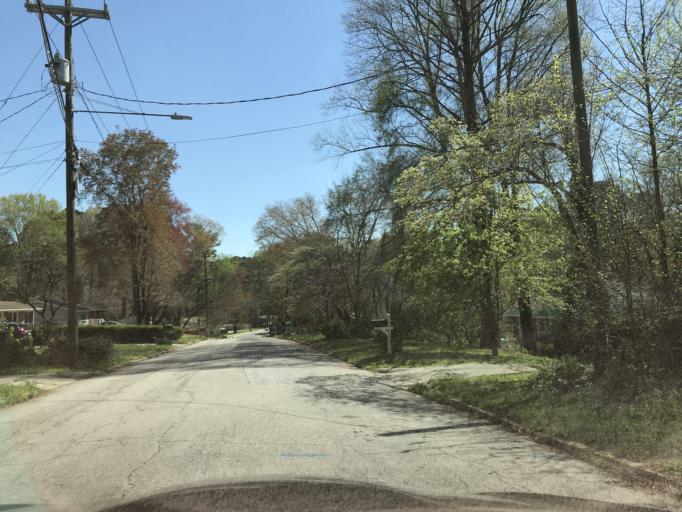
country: US
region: North Carolina
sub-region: Wake County
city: West Raleigh
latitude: 35.7729
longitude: -78.7082
